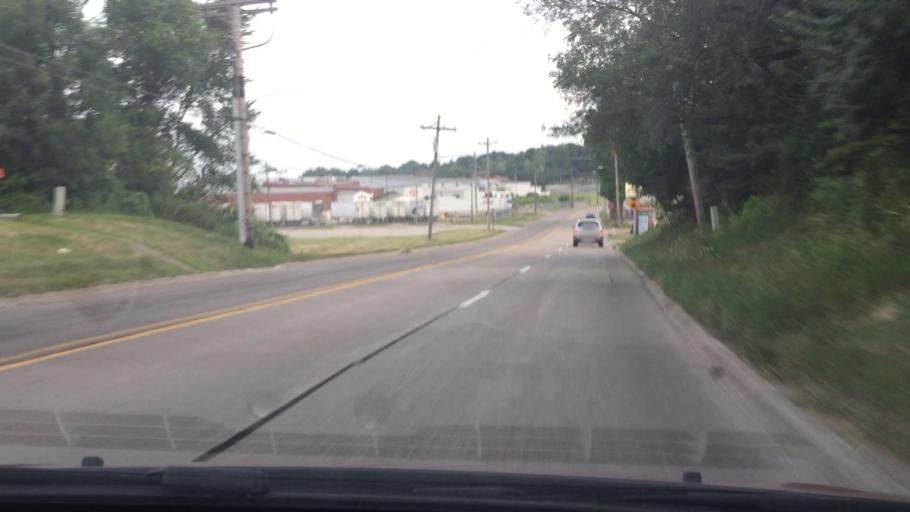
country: US
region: Iowa
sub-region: Muscatine County
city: Muscatine
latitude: 41.4424
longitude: -91.0419
